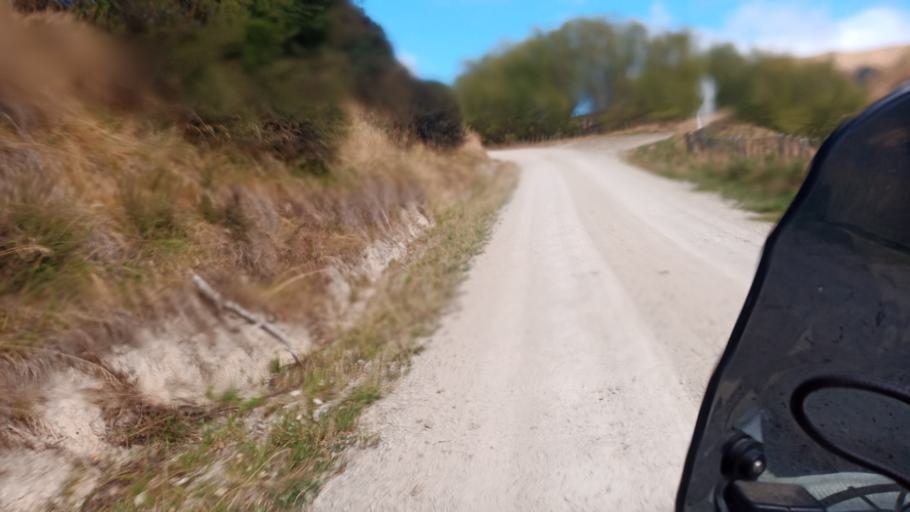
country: NZ
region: Hawke's Bay
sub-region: Wairoa District
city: Wairoa
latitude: -38.6028
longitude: 177.4860
